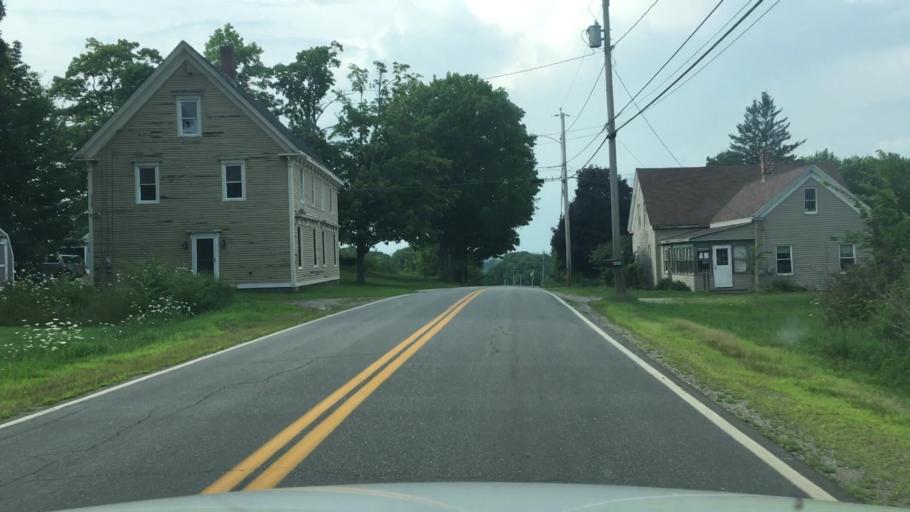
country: US
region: Maine
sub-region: Lincoln County
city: Jefferson
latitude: 44.1836
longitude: -69.3755
